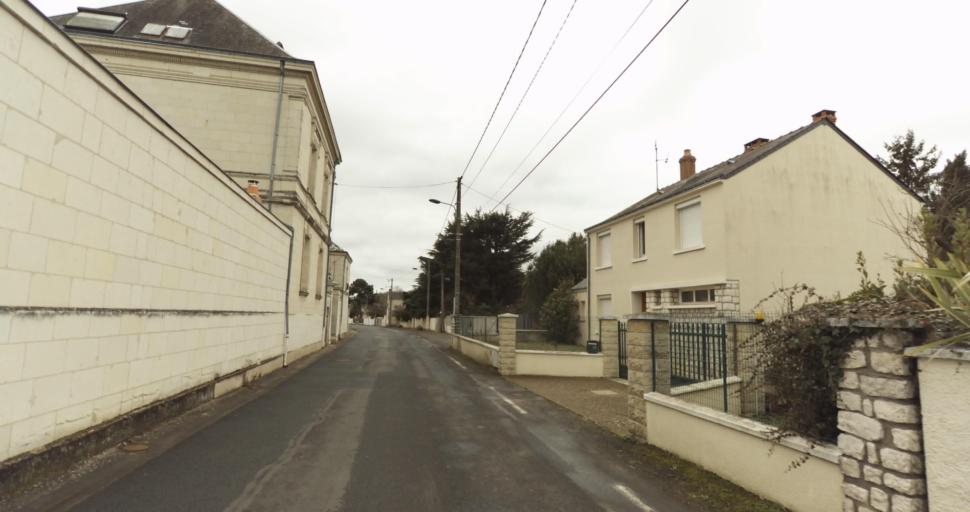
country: FR
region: Pays de la Loire
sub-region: Departement de Maine-et-Loire
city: Distre
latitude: 47.2381
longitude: -0.0939
